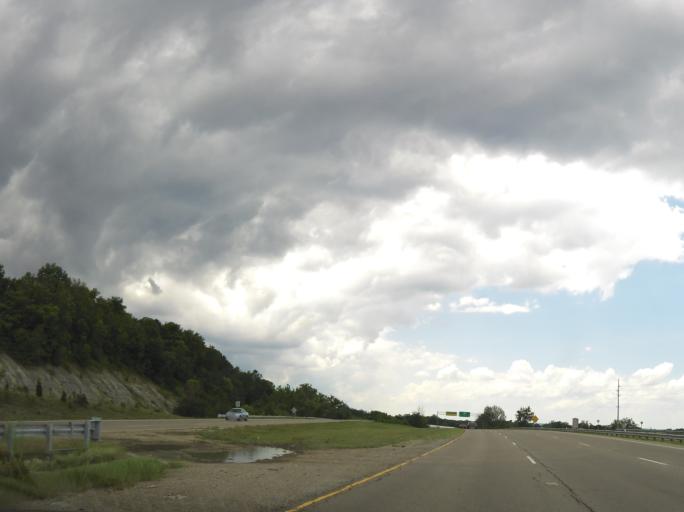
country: US
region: Ohio
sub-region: Greene County
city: Wright-Patterson AFB
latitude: 39.7966
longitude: -84.0881
